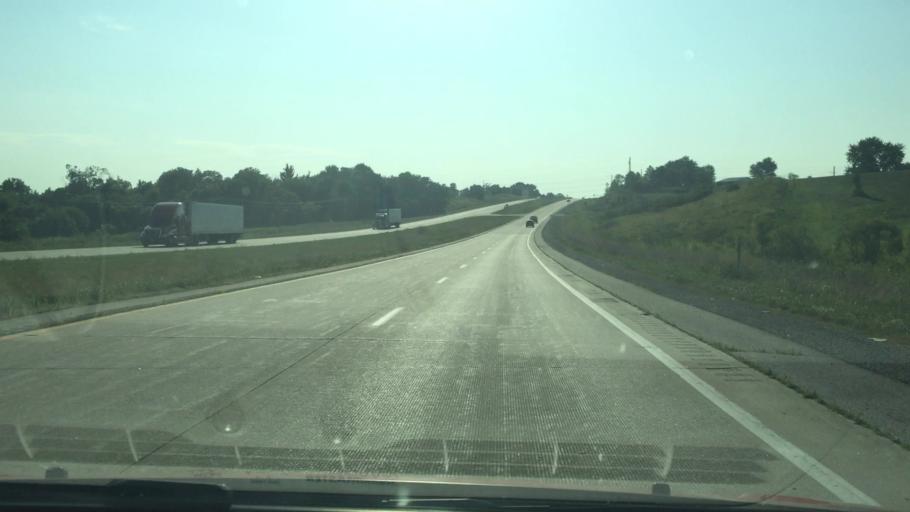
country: US
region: Iowa
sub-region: Scott County
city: Blue Grass
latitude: 41.5130
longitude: -90.8004
